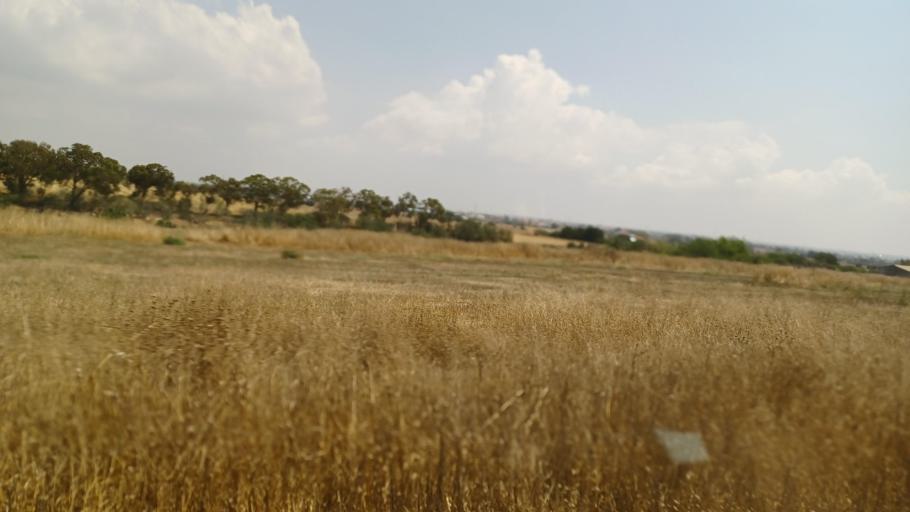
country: CY
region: Ammochostos
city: Liopetri
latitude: 34.9852
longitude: 33.8628
